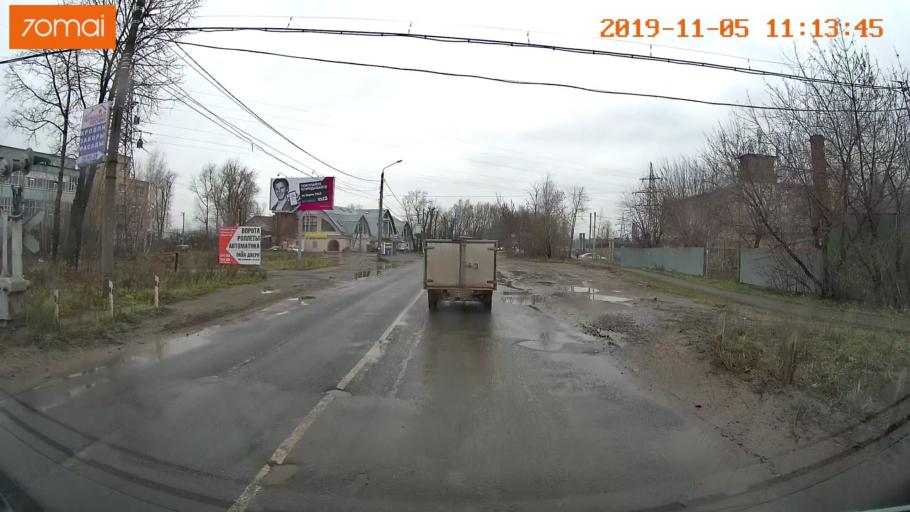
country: RU
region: Ivanovo
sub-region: Gorod Ivanovo
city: Ivanovo
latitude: 56.9673
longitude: 40.9523
